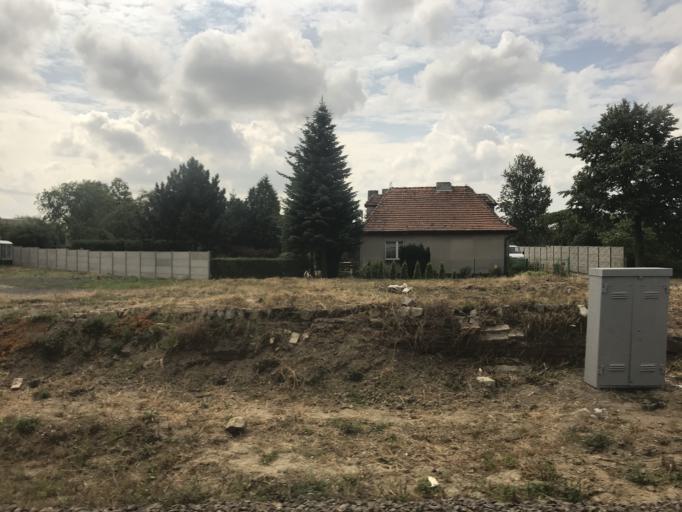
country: PL
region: Greater Poland Voivodeship
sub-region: Powiat gnieznienski
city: Lubowo
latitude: 52.5056
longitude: 17.4804
